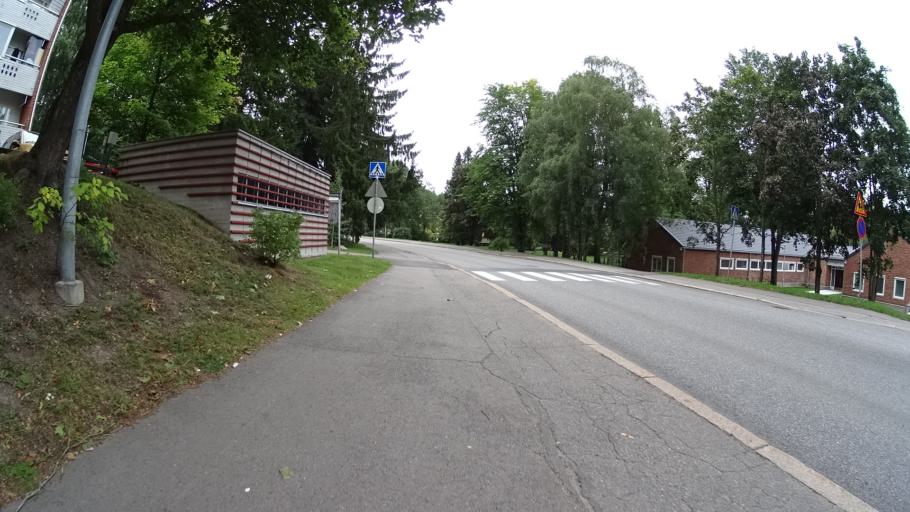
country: FI
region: Uusimaa
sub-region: Helsinki
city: Helsinki
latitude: 60.2287
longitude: 24.9240
